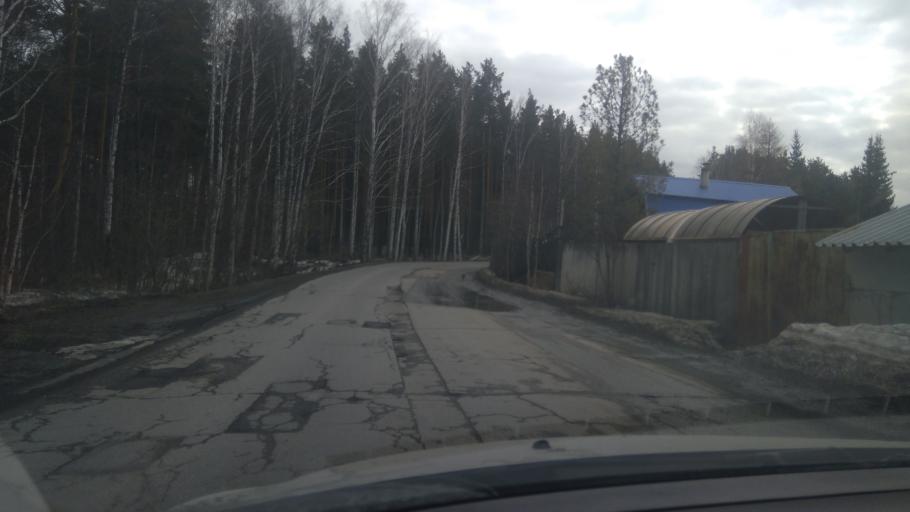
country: RU
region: Sverdlovsk
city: Severka
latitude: 56.8412
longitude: 60.3855
